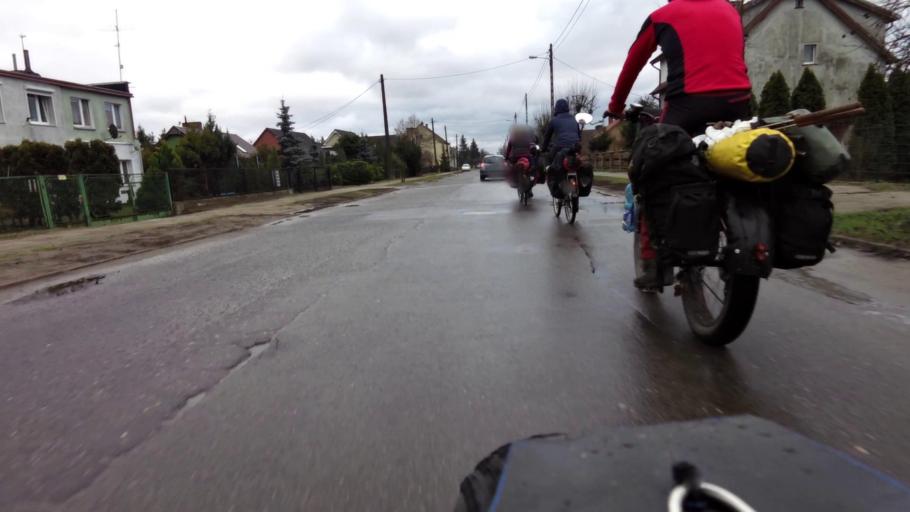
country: PL
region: Lubusz
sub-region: Powiat gorzowski
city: Witnica
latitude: 52.6815
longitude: 14.8904
